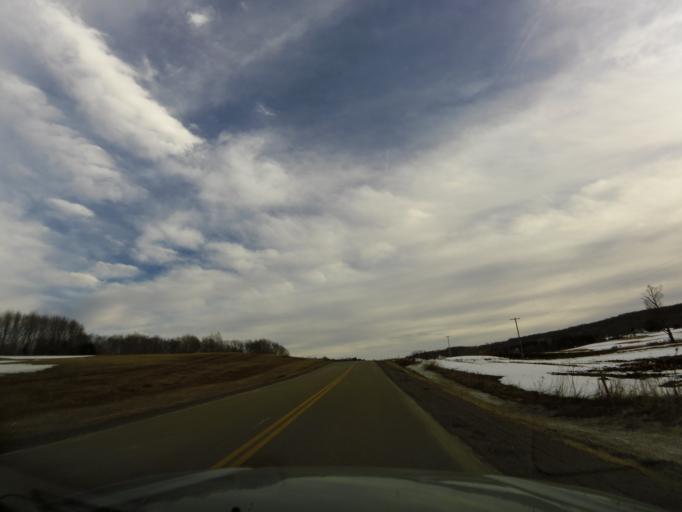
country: US
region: New York
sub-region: Cattaraugus County
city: Delevan
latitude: 42.5113
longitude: -78.5088
